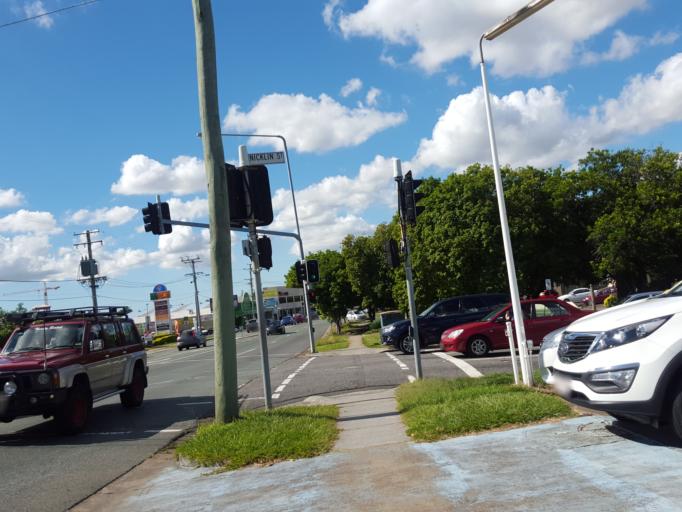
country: AU
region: Queensland
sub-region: Brisbane
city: Greenslopes
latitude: -27.4976
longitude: 153.0539
